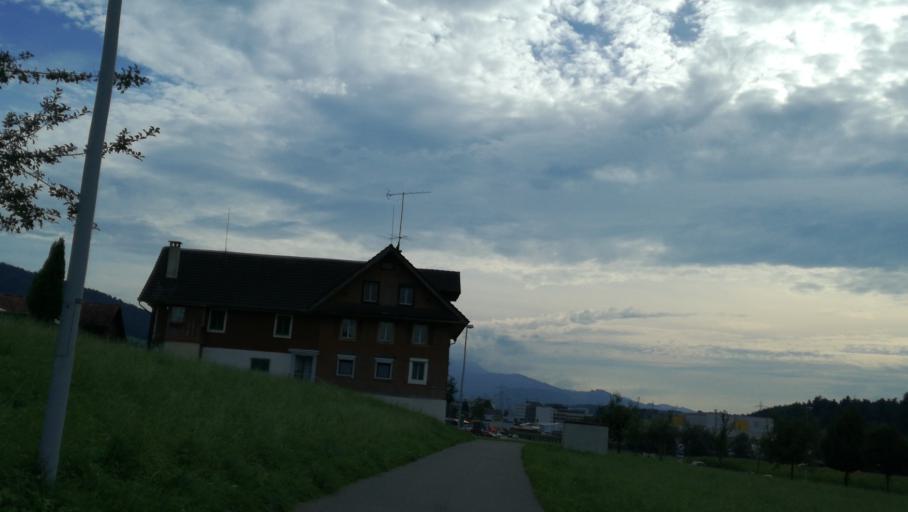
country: CH
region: Lucerne
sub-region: Lucerne-Land District
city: Root
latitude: 47.1088
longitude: 8.3842
